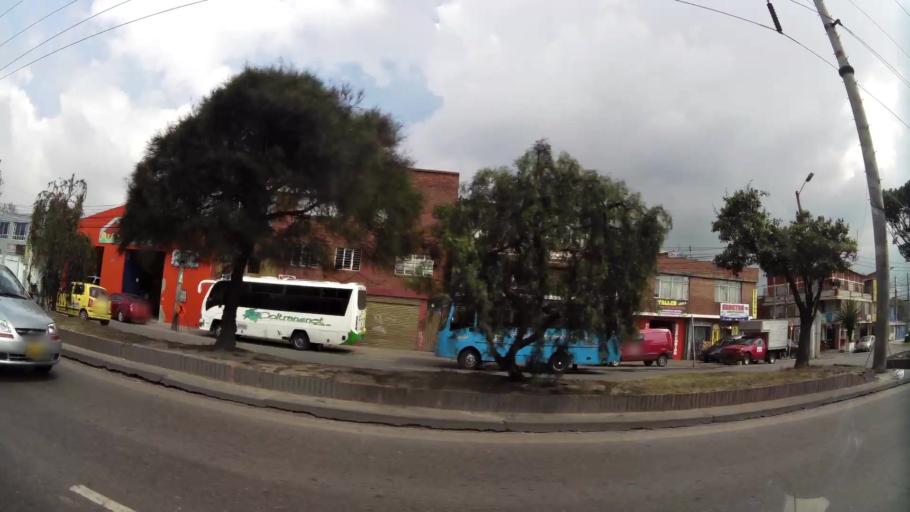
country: CO
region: Bogota D.C.
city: Bogota
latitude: 4.5919
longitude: -74.1162
